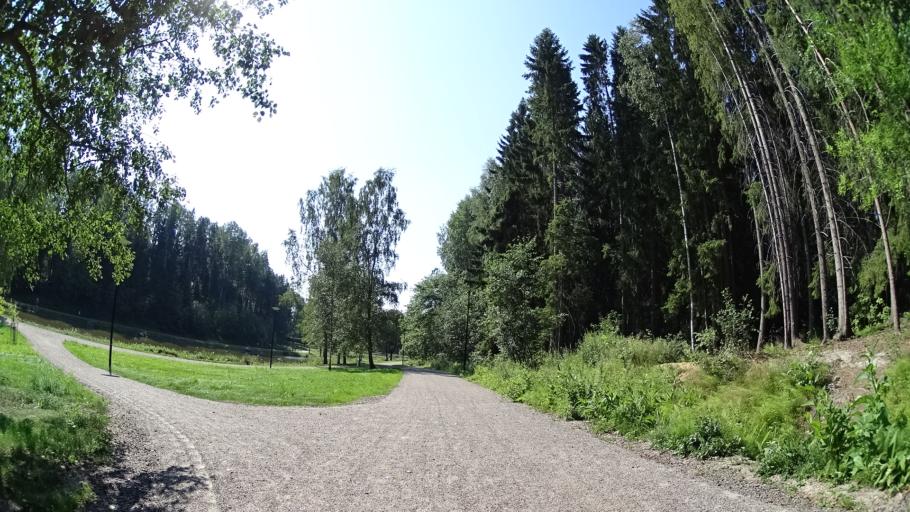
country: FI
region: Uusimaa
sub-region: Helsinki
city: Kerava
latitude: 60.3556
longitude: 25.0726
